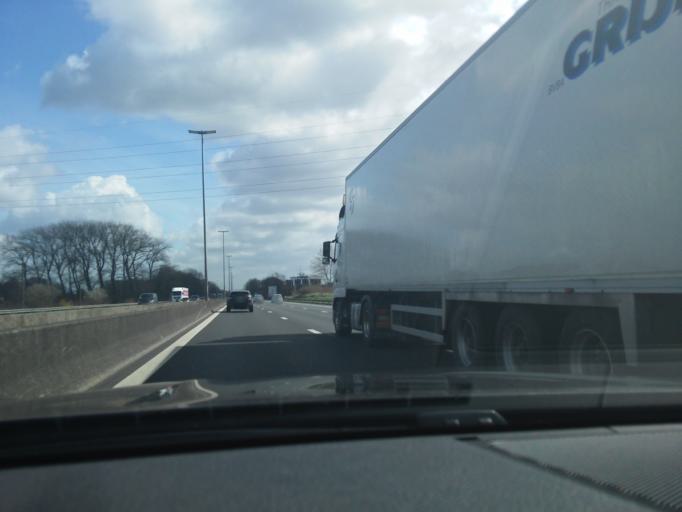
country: BE
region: Flanders
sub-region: Provincie Oost-Vlaanderen
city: Sint-Martens-Latem
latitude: 51.0435
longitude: 3.6018
